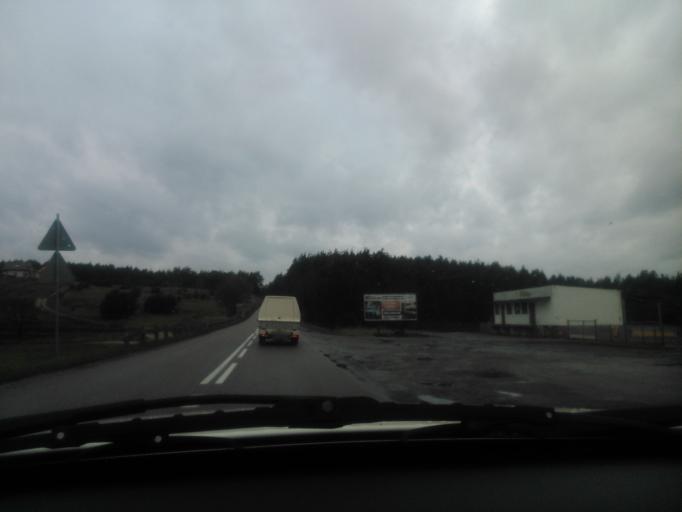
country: PL
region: Warmian-Masurian Voivodeship
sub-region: Powiat dzialdowski
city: Lidzbark
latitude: 53.2688
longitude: 19.8165
